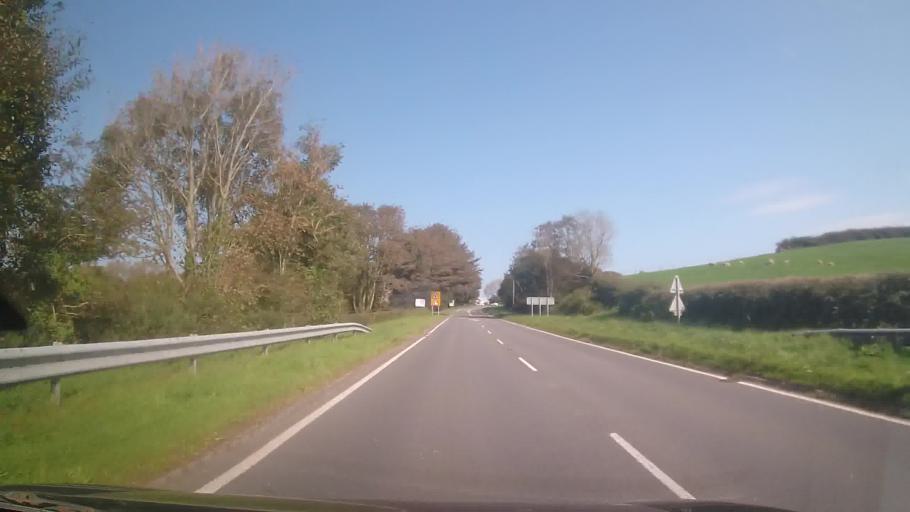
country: GB
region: Wales
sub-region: Pembrokeshire
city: Nevern
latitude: 52.0167
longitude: -4.7976
